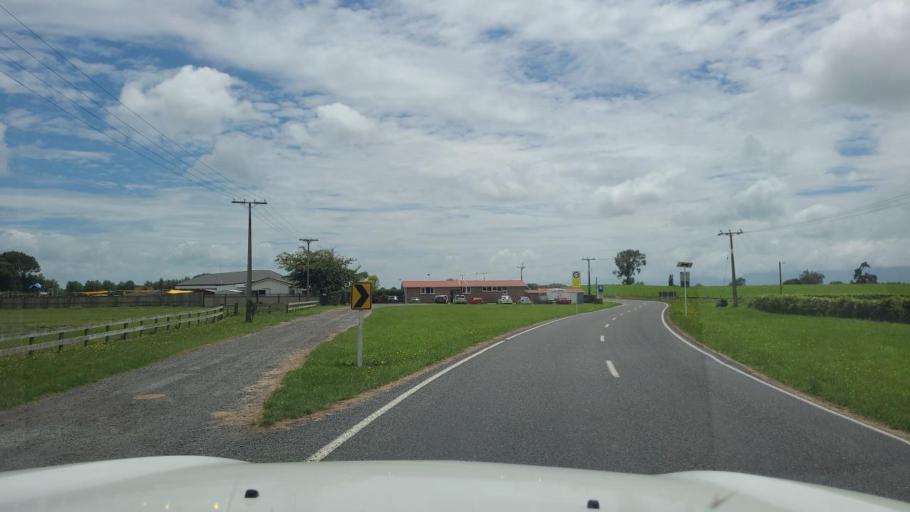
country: NZ
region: Waikato
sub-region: Matamata-Piako District
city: Matamata
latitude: -37.8796
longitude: 175.7585
